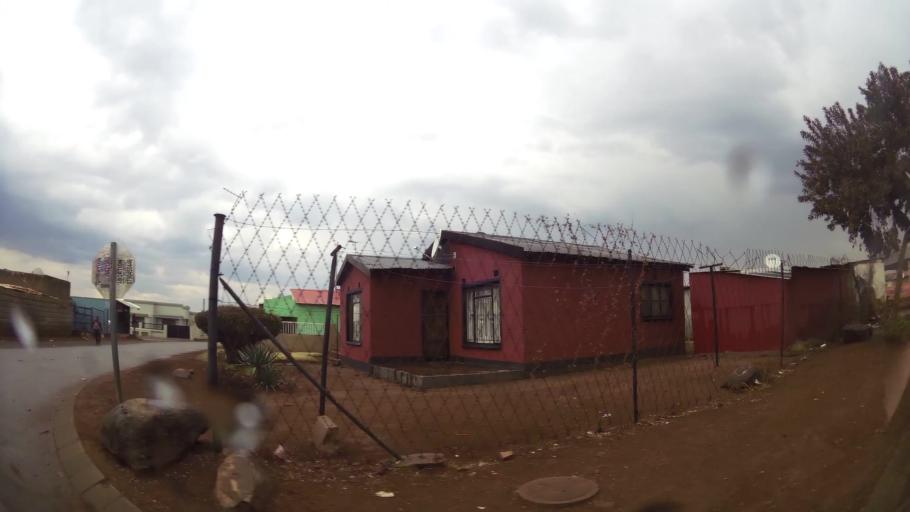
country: ZA
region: Gauteng
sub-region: Ekurhuleni Metropolitan Municipality
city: Germiston
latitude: -26.3654
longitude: 28.1370
